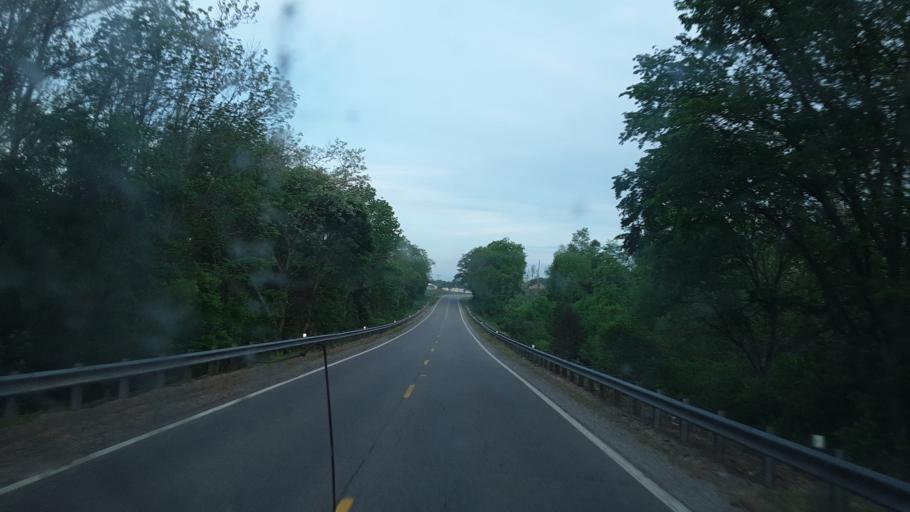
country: US
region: Ohio
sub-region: Ross County
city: Kingston
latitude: 39.4538
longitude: -82.7763
